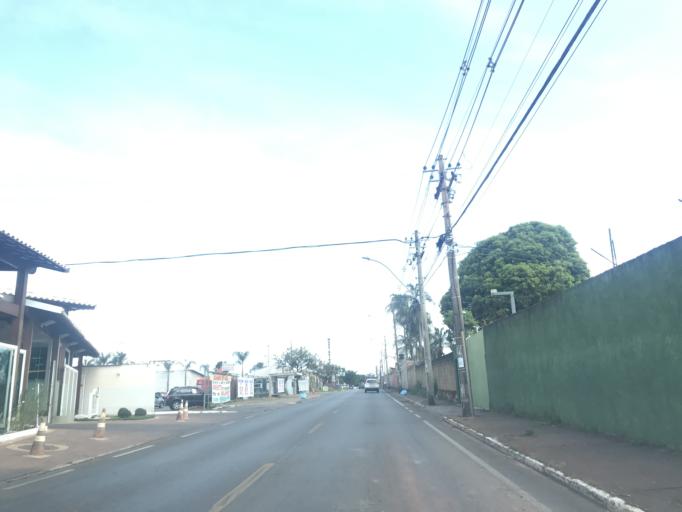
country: BR
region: Federal District
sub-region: Brasilia
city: Brasilia
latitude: -15.8798
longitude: -47.8201
